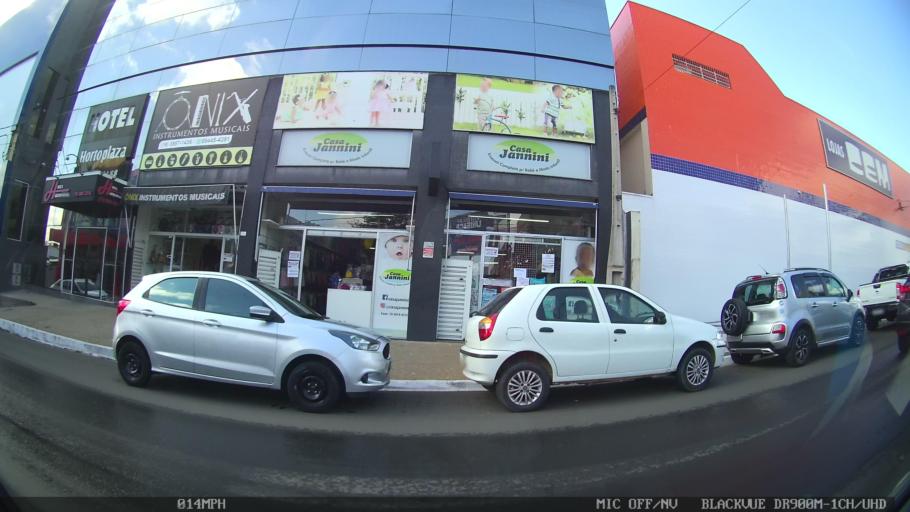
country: BR
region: Sao Paulo
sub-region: Hortolandia
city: Hortolandia
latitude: -22.8641
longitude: -47.2170
